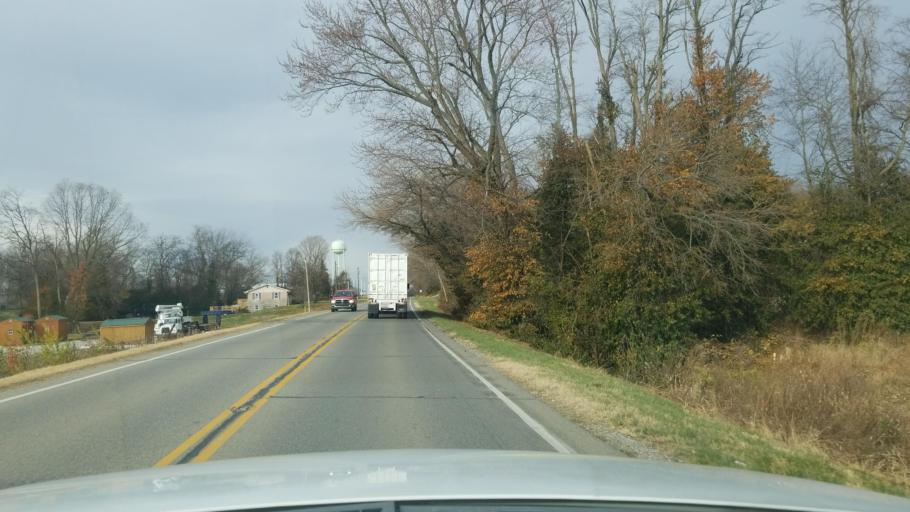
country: US
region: Indiana
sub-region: Posey County
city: Mount Vernon
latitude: 37.9279
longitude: -87.9161
